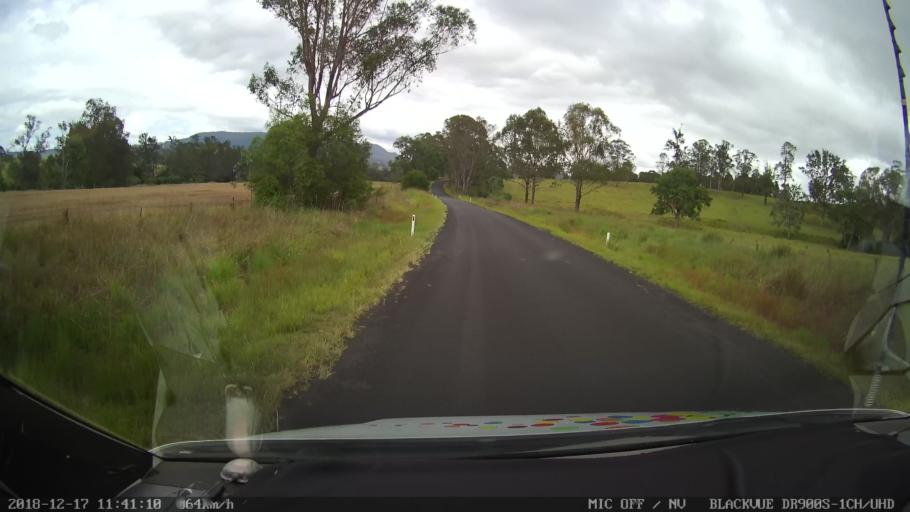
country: AU
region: New South Wales
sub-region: Kyogle
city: Kyogle
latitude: -28.6765
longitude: 152.5901
